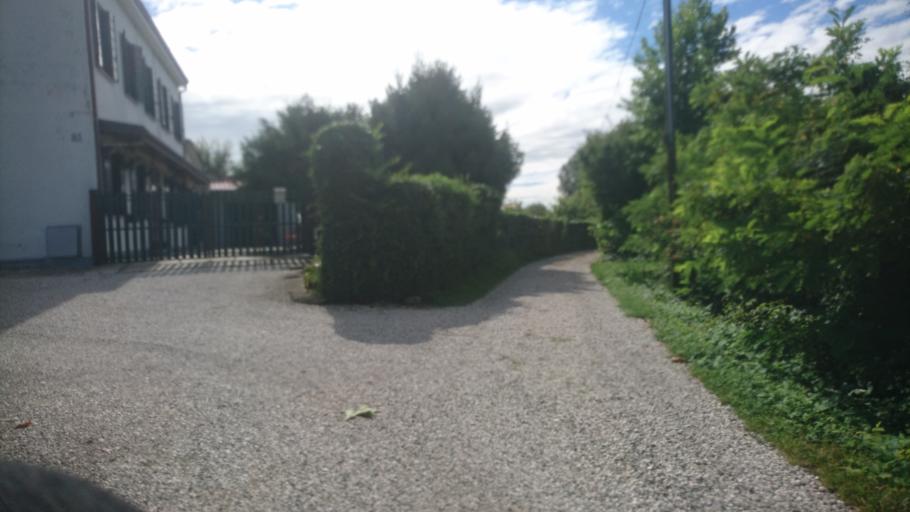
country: IT
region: Veneto
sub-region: Provincia di Padova
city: Albignasego
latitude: 45.3576
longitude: 11.8739
